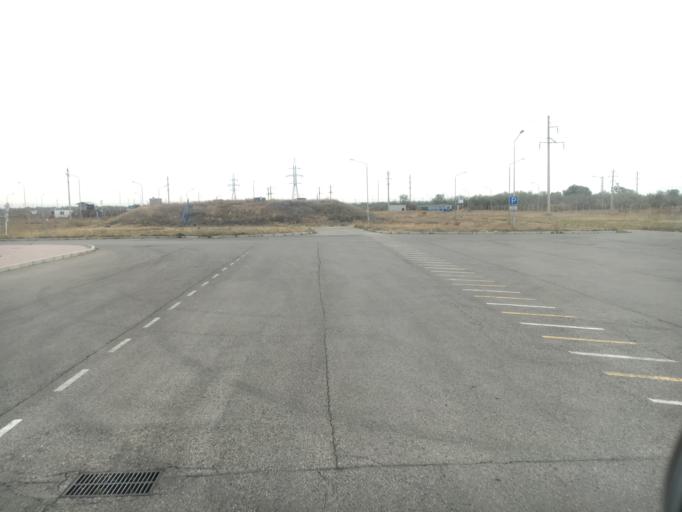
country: KZ
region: Almaty Oblysy
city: Energeticheskiy
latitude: 43.5853
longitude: 77.0940
